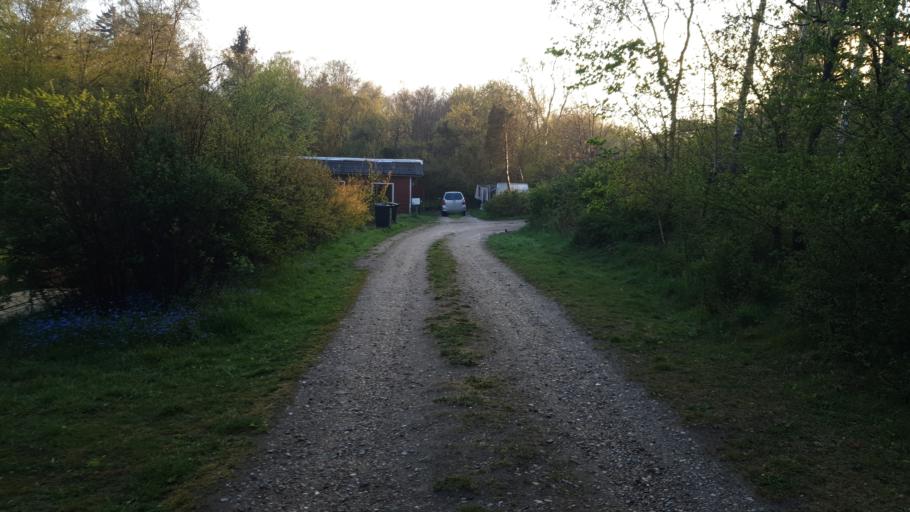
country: DK
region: Zealand
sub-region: Odsherred Kommune
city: Hojby
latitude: 55.9365
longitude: 11.6196
